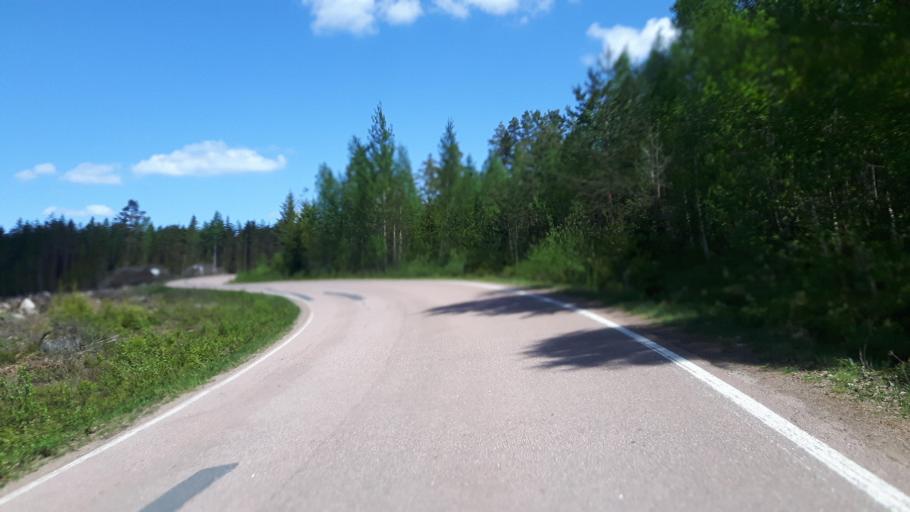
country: FI
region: Kymenlaakso
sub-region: Kotka-Hamina
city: Virolahti
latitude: 60.5420
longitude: 27.6337
